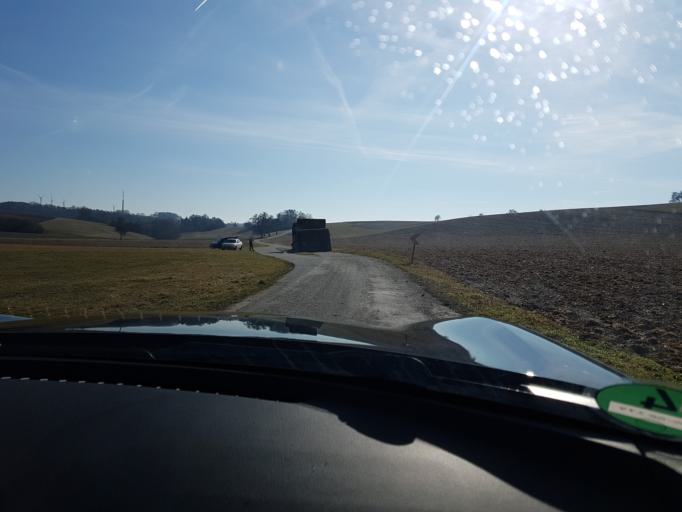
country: DE
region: Baden-Wuerttemberg
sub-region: Karlsruhe Region
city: Rosenberg
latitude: 49.4127
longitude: 9.5016
